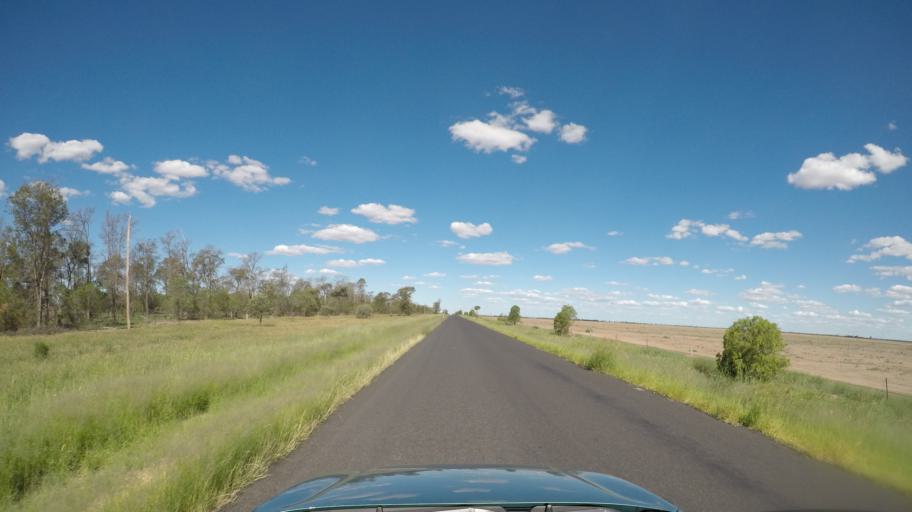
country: AU
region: Queensland
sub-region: Goondiwindi
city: Goondiwindi
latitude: -28.1627
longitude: 150.1508
